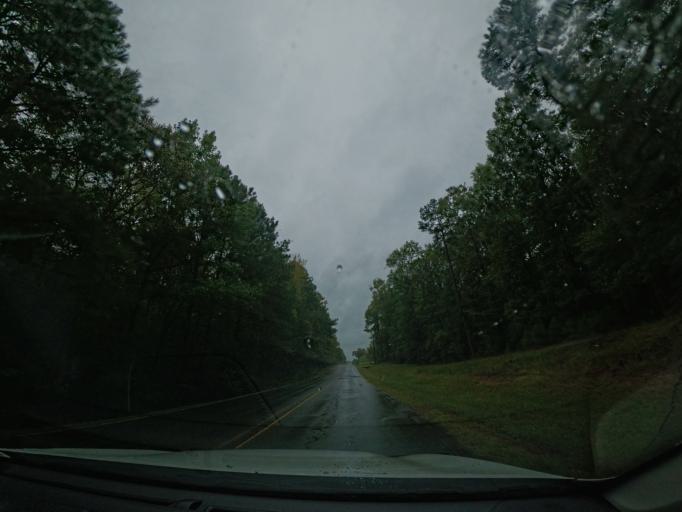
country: US
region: Louisiana
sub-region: Webster Parish
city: Minden
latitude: 32.6352
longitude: -93.2498
